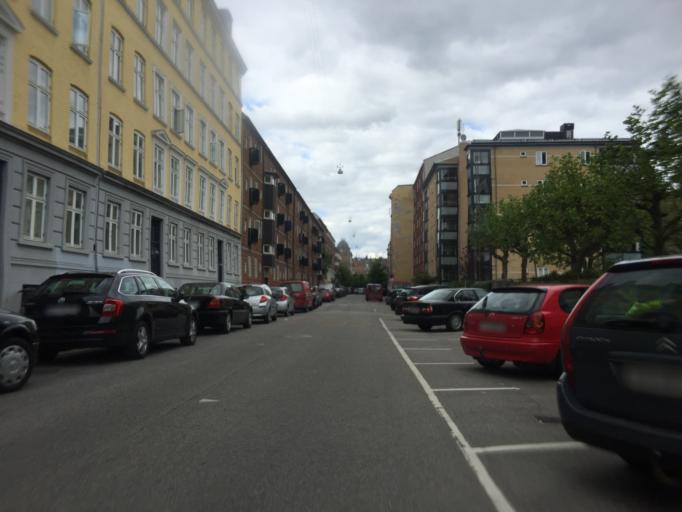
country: DK
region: Capital Region
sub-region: Frederiksberg Kommune
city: Frederiksberg
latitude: 55.6716
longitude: 12.5385
